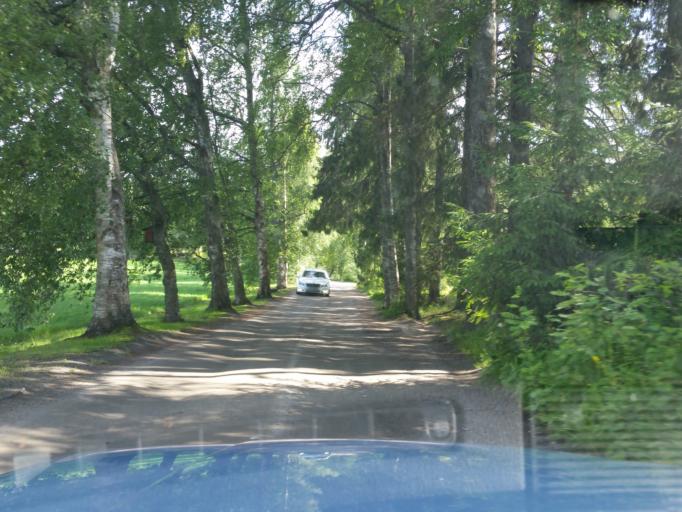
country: FI
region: Southern Savonia
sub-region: Mikkeli
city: Mikkeli
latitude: 61.7058
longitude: 27.3819
